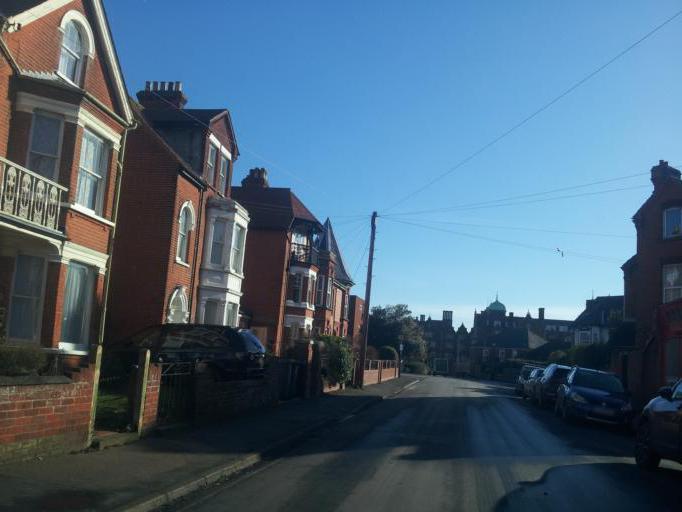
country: GB
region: England
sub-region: Suffolk
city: Felixstowe
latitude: 51.9631
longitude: 1.3550
